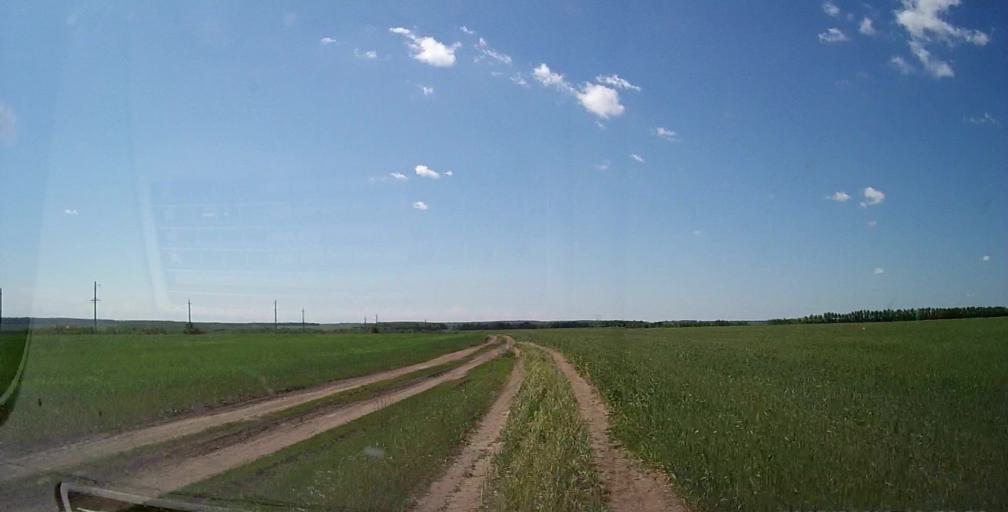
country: RU
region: Tula
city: Kurkino
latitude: 53.1583
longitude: 38.4815
